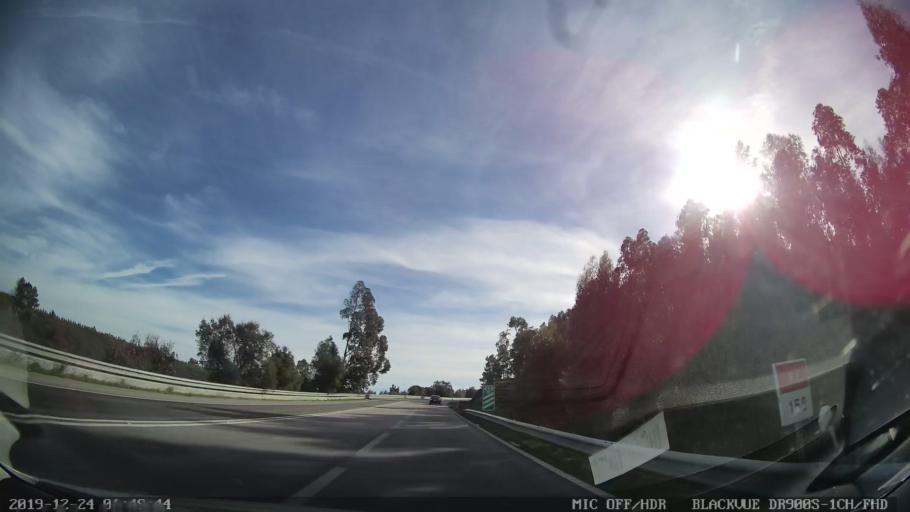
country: PT
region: Portalegre
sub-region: Nisa
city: Nisa
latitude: 39.5041
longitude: -7.7698
